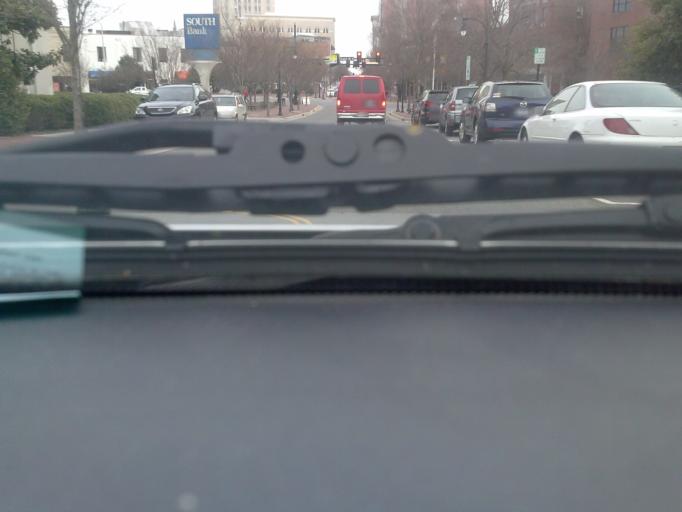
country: US
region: North Carolina
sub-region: Durham County
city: Durham
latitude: 35.9975
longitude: -78.9049
